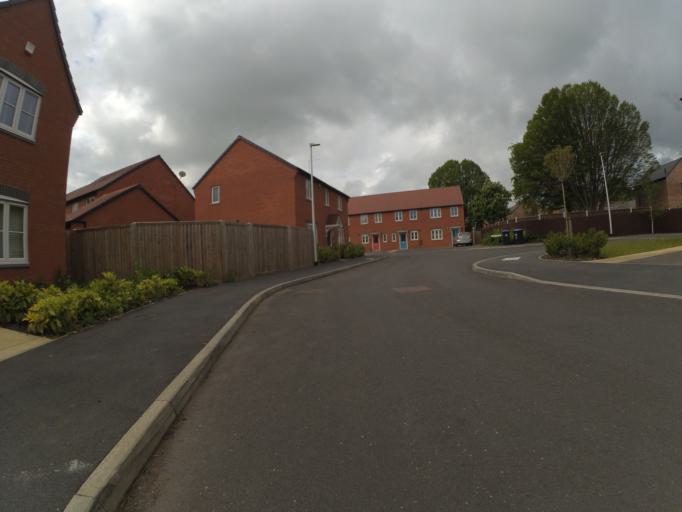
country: GB
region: England
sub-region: Warwickshire
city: Rugby
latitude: 52.3692
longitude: -1.2433
